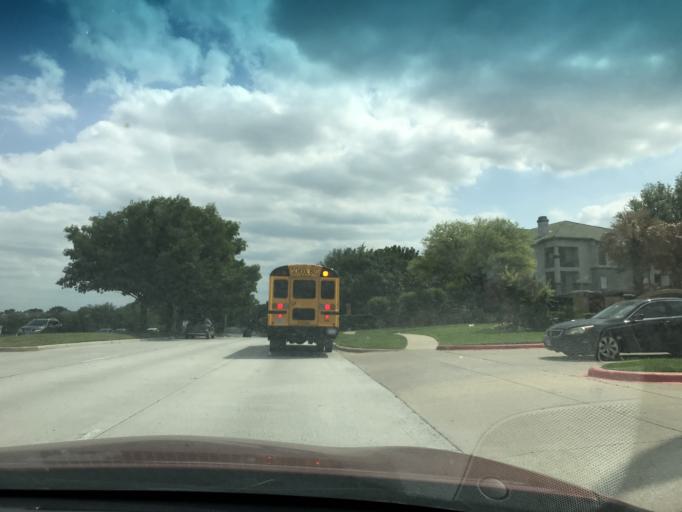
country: US
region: Texas
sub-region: Tarrant County
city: Benbrook
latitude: 32.6744
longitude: -97.4185
